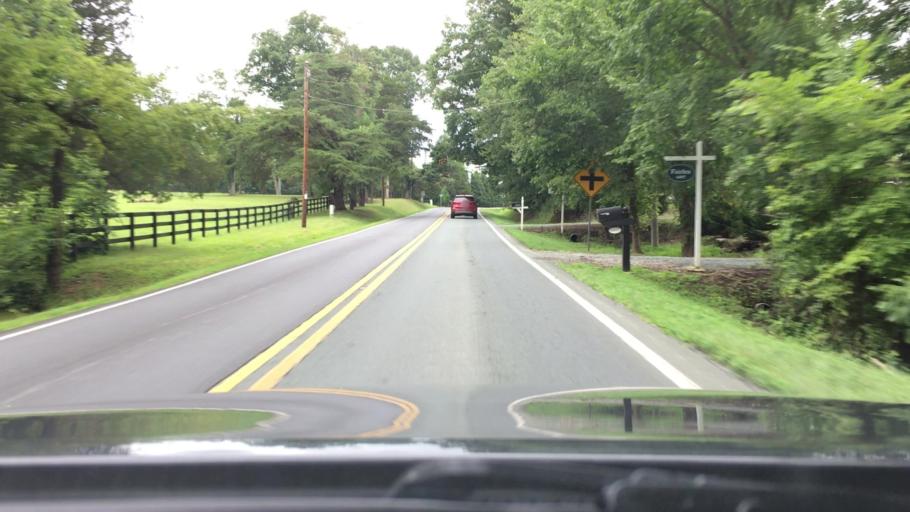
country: US
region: Virginia
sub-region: Orange County
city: Gordonsville
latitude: 38.0872
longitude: -78.2785
